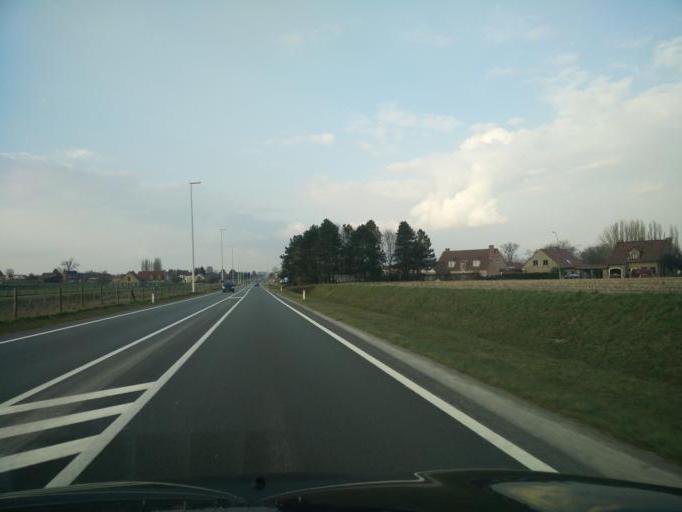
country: BE
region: Flanders
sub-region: Provincie Oost-Vlaanderen
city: Oosterzele
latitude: 50.9162
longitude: 3.8177
